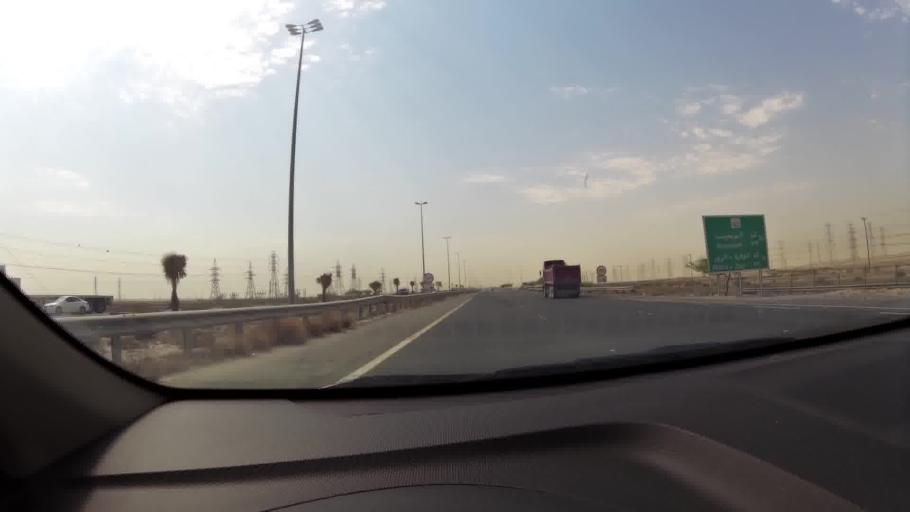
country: KW
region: Al Ahmadi
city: Al Fahahil
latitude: 28.8537
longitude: 48.2428
